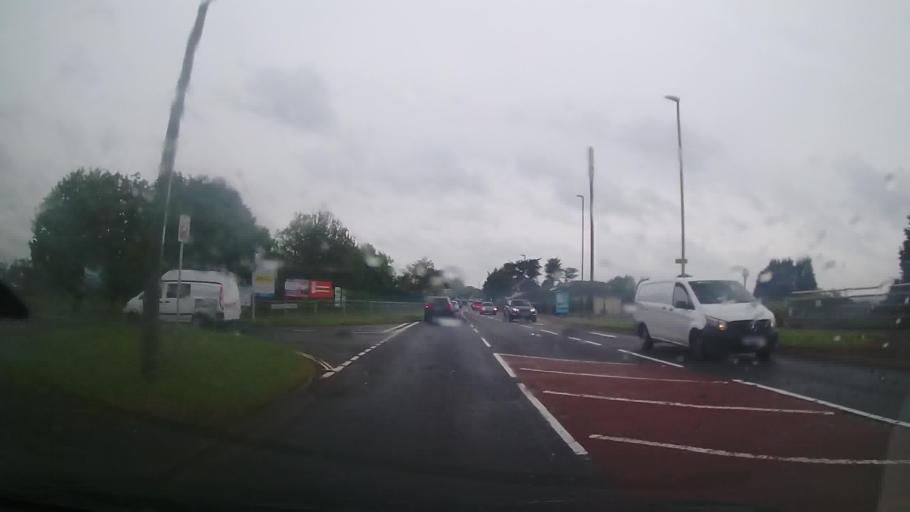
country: GB
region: England
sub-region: Borough of Torbay
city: Brixham
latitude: 50.3969
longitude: -3.5562
